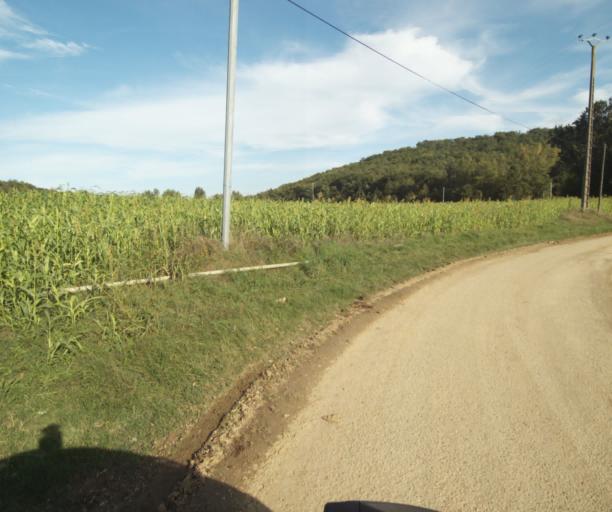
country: FR
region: Midi-Pyrenees
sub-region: Departement du Tarn-et-Garonne
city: Saint-Porquier
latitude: 43.9373
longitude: 1.1449
